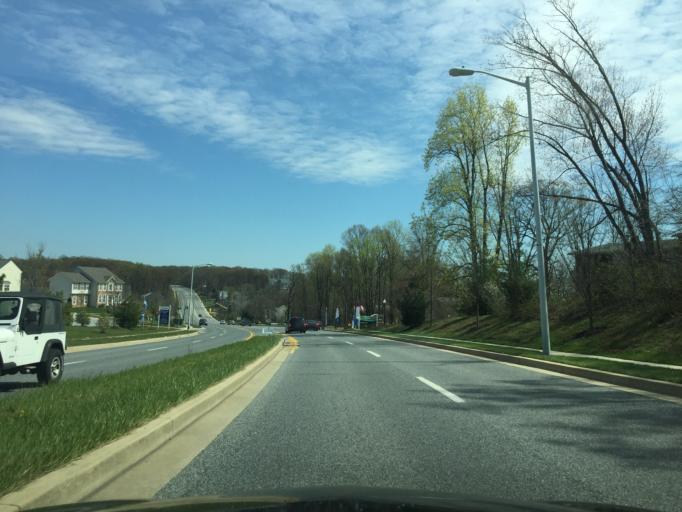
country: US
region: Maryland
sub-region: Baltimore County
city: Overlea
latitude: 39.3604
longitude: -76.4998
